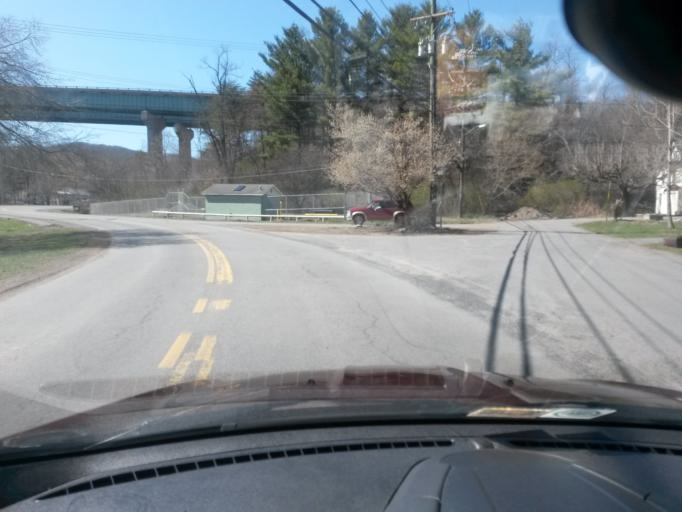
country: US
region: West Virginia
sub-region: Greenbrier County
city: White Sulphur Springs
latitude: 37.7914
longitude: -80.2913
